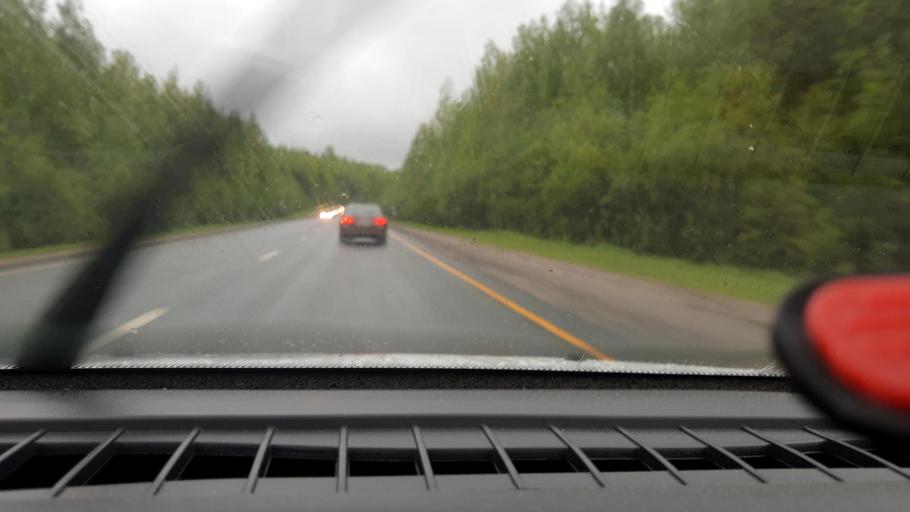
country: RU
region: Nizjnij Novgorod
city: Semenov
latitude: 56.7541
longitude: 44.3625
